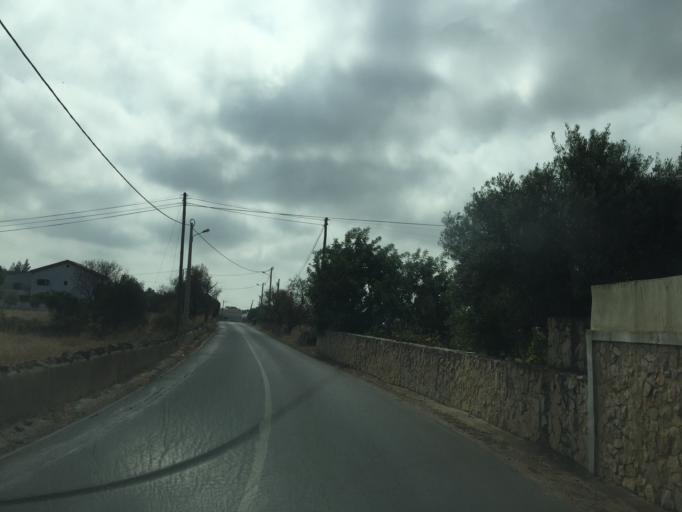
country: PT
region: Faro
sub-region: Olhao
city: Olhao
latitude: 37.0723
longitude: -7.8860
